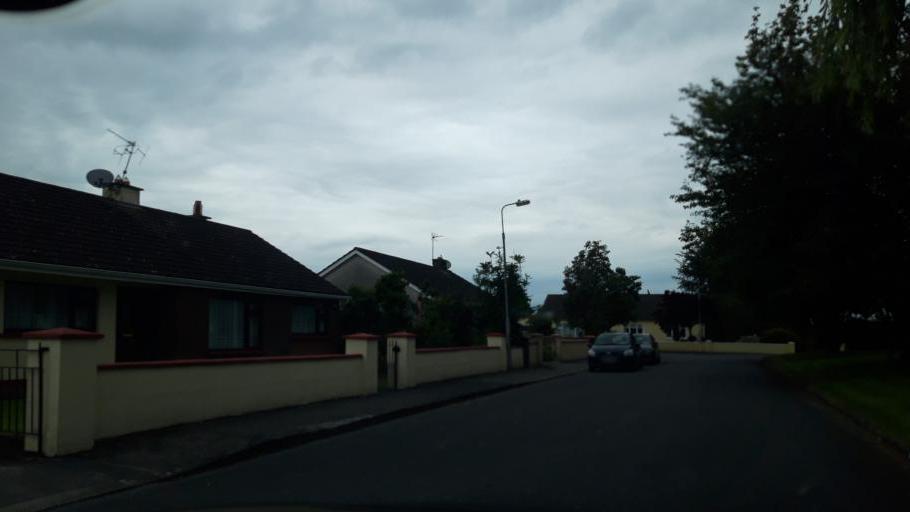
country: IE
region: Leinster
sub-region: Kilkenny
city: Ballyragget
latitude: 52.7824
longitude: -7.3310
